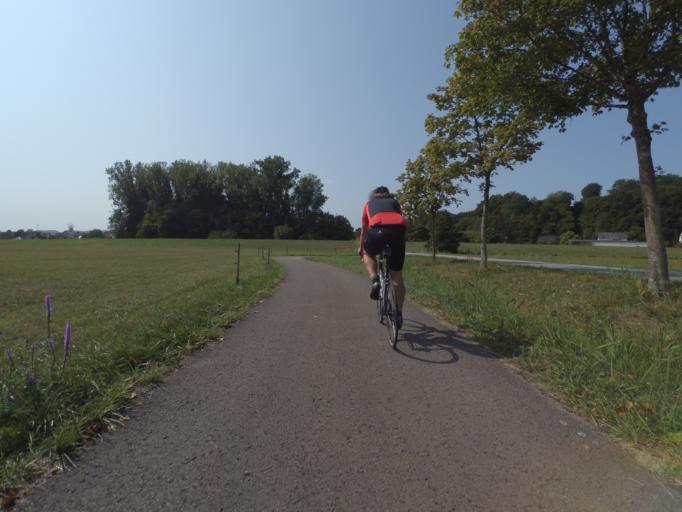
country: DE
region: Saarland
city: Mettlach
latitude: 49.4723
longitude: 6.5906
